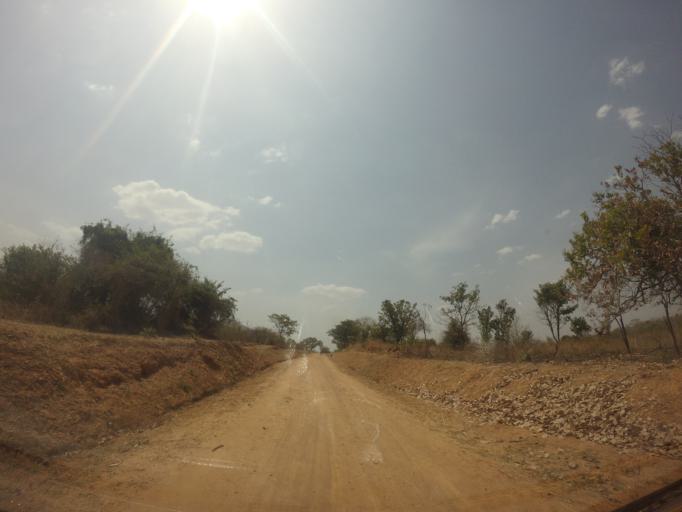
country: UG
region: Northern Region
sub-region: Arua District
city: Arua
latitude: 2.8968
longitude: 31.1162
